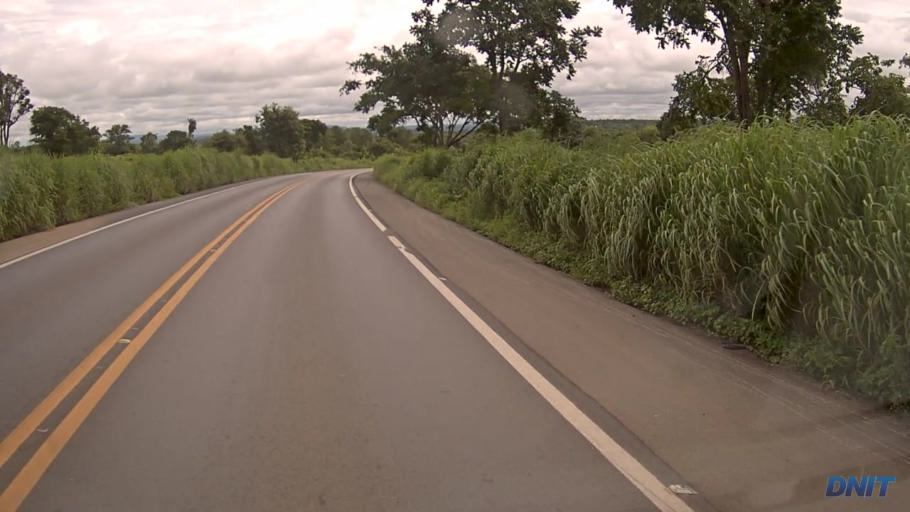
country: BR
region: Goias
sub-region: Posse
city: Posse
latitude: -14.3244
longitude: -46.4431
